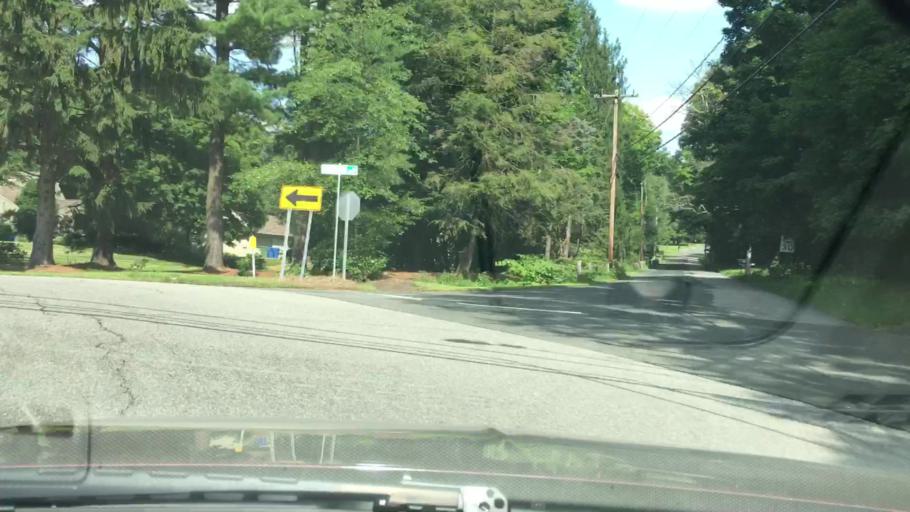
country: US
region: Connecticut
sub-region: Hartford County
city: Manchester
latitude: 41.7302
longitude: -72.5178
